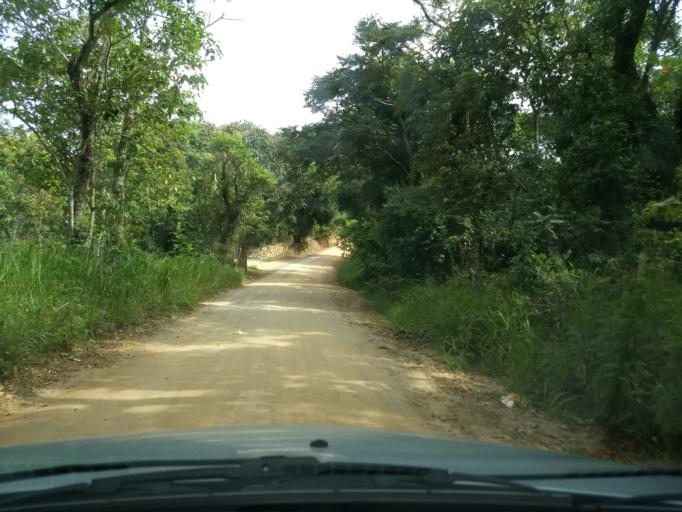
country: BR
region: Minas Gerais
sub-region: Extrema
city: Extrema
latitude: -22.8545
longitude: -46.3972
